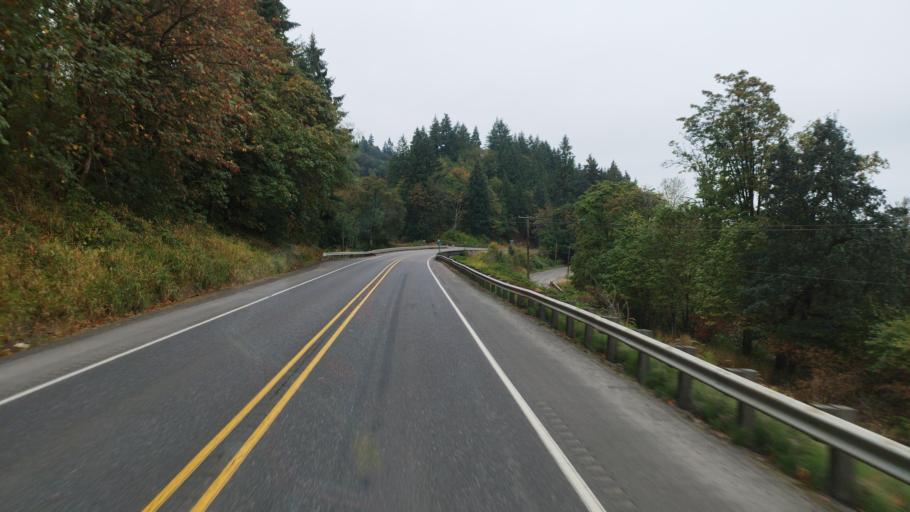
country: US
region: Washington
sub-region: Cowlitz County
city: Kalama
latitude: 45.9591
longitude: -122.8673
